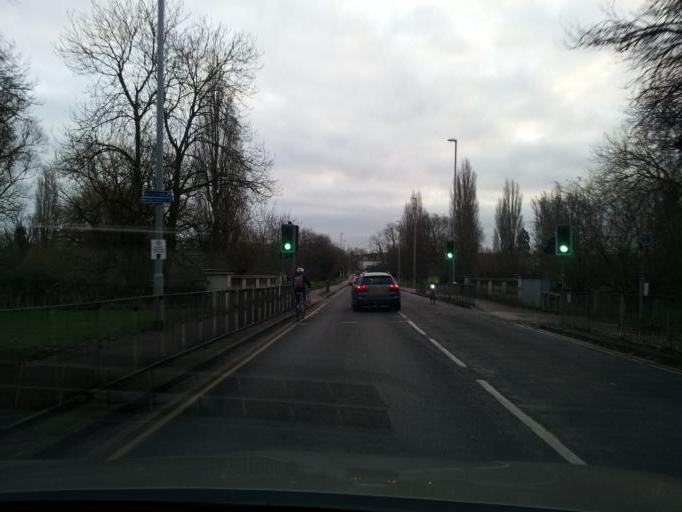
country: GB
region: England
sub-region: Cambridgeshire
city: Cambridge
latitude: 52.1980
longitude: 0.1142
